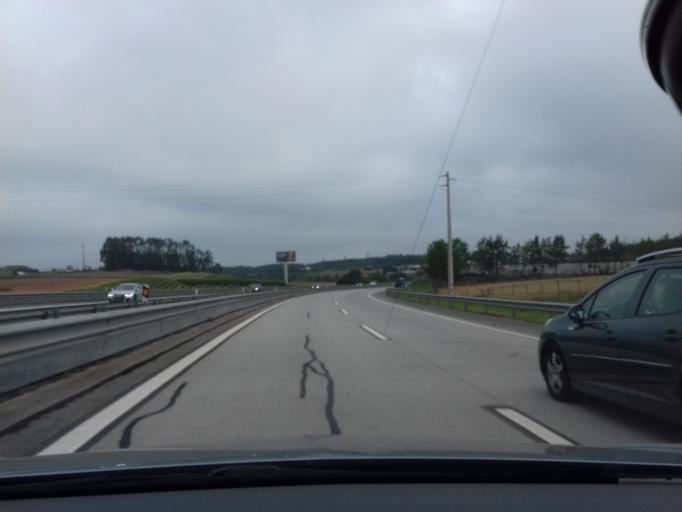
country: PT
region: Leiria
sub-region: Bombarral
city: Bombarral
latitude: 39.1886
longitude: -9.2061
